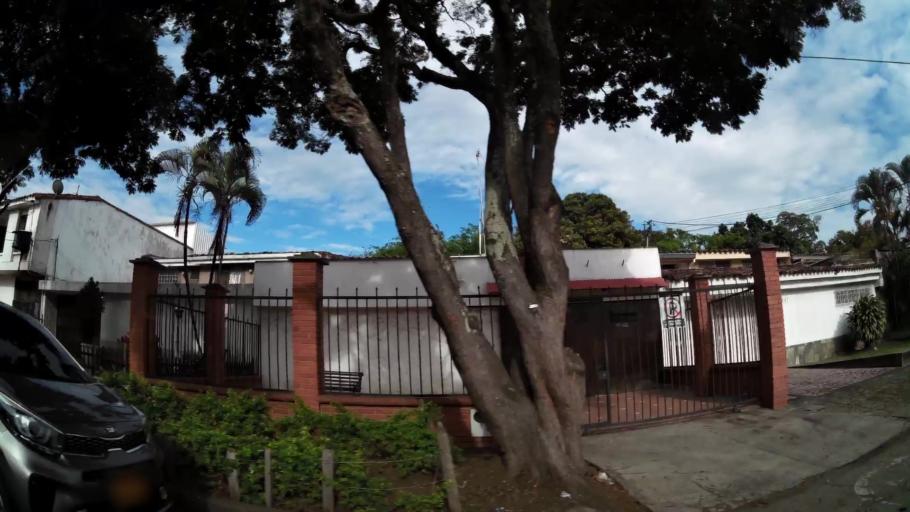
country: CO
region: Valle del Cauca
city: Cali
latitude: 3.4839
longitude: -76.5223
